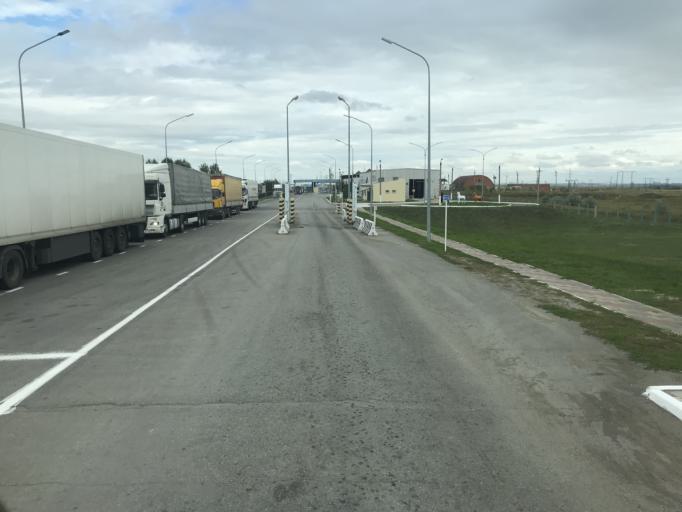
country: RU
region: Chelyabinsk
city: Bobrovka
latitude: 53.9987
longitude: 61.6418
